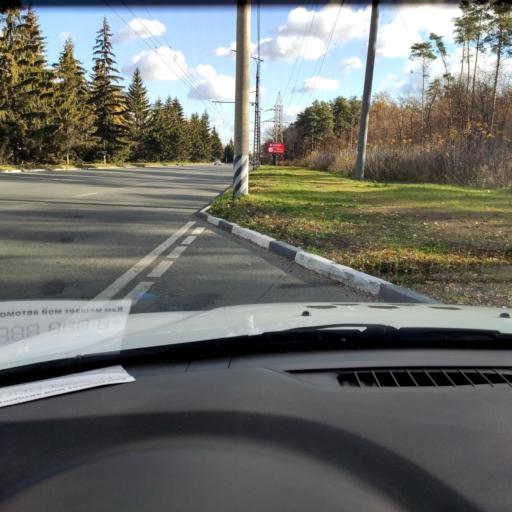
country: RU
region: Samara
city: Tol'yatti
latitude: 53.5060
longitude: 49.4406
